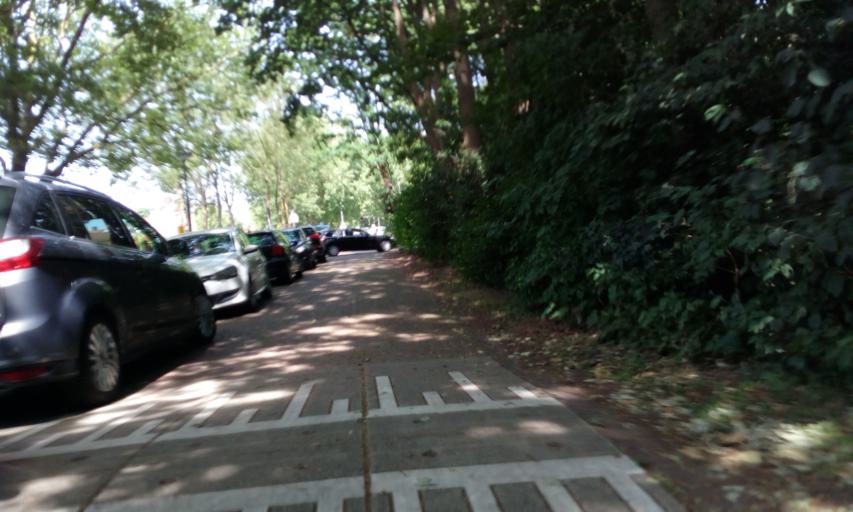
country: NL
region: South Holland
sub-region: Gemeente Lansingerland
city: Bergschenhoek
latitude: 51.9546
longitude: 4.5135
